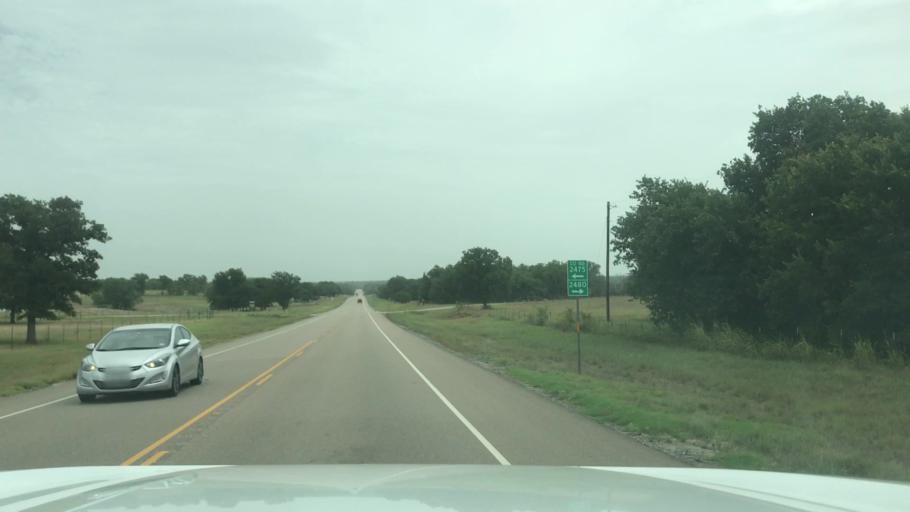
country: US
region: Texas
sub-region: Hamilton County
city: Hico
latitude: 31.9782
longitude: -97.9125
